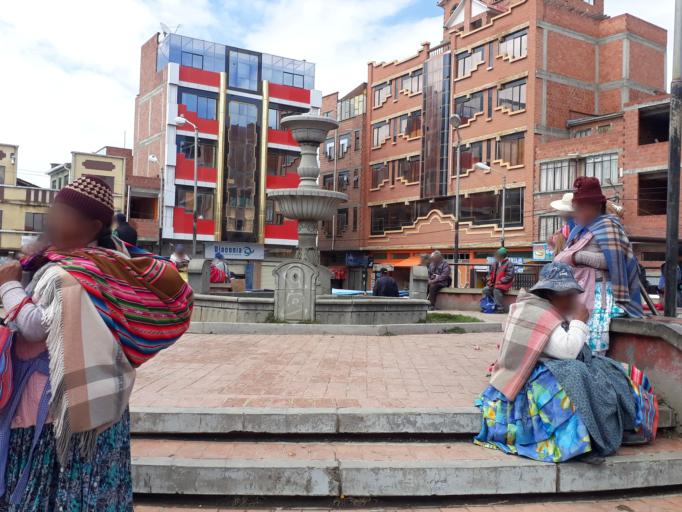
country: BO
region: La Paz
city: Achacachi
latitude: -16.0447
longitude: -68.6853
